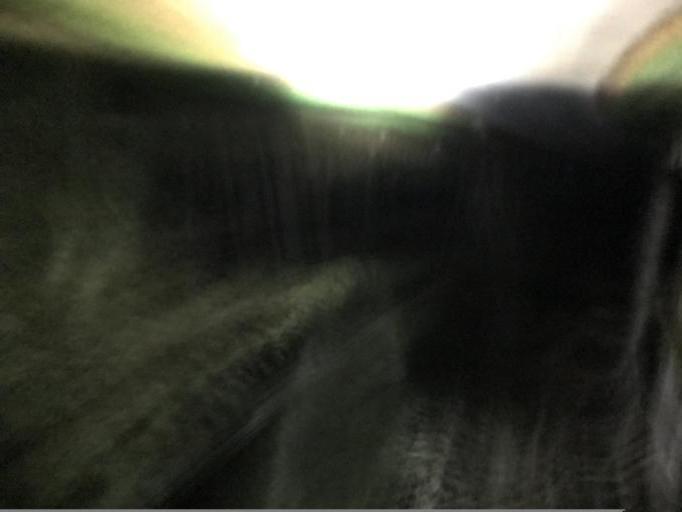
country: FR
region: Auvergne
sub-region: Departement du Puy-de-Dome
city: Celles-sur-Durolle
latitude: 45.8569
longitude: 3.6241
